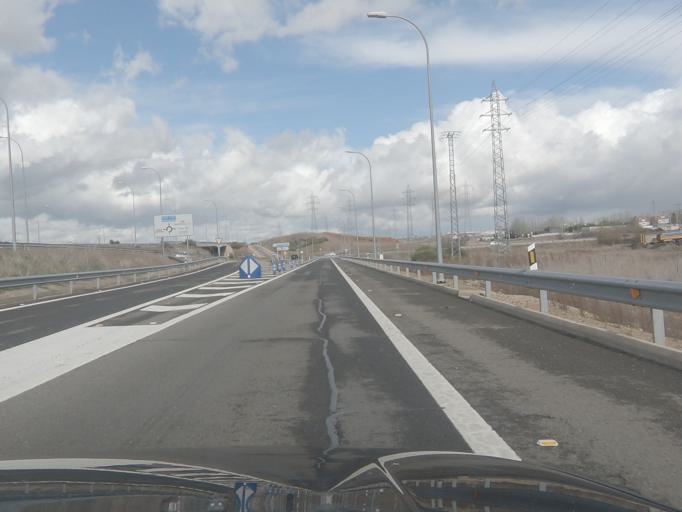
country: ES
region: Castille and Leon
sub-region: Provincia de Salamanca
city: Villares de la Reina
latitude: 40.9974
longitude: -5.6694
